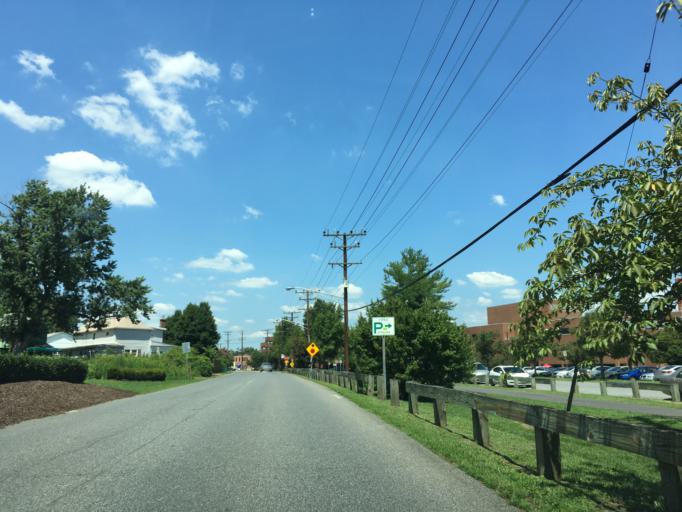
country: US
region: Maryland
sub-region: Anne Arundel County
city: Glen Burnie
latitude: 39.1612
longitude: -76.6230
